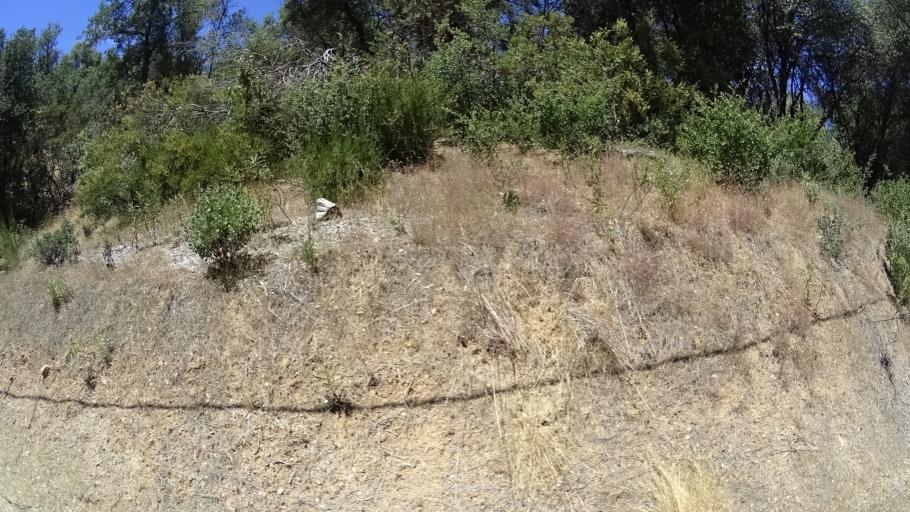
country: US
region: California
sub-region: Calaveras County
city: Mountain Ranch
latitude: 38.2415
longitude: -120.5077
